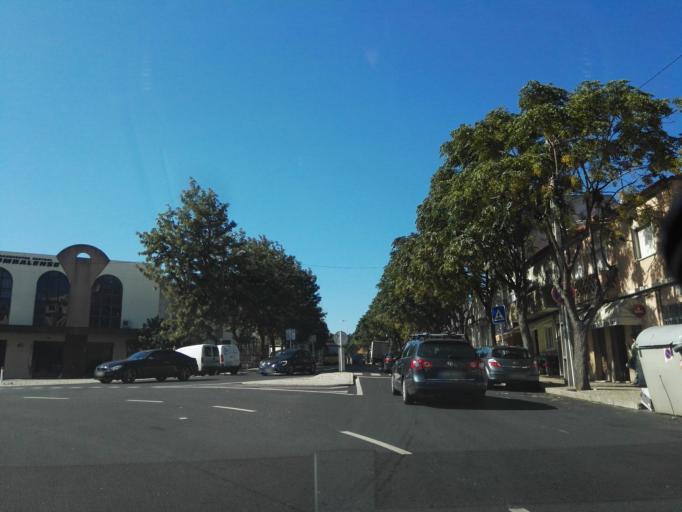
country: PT
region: Lisbon
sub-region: Loures
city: Camarate
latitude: 38.7900
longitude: -9.1231
